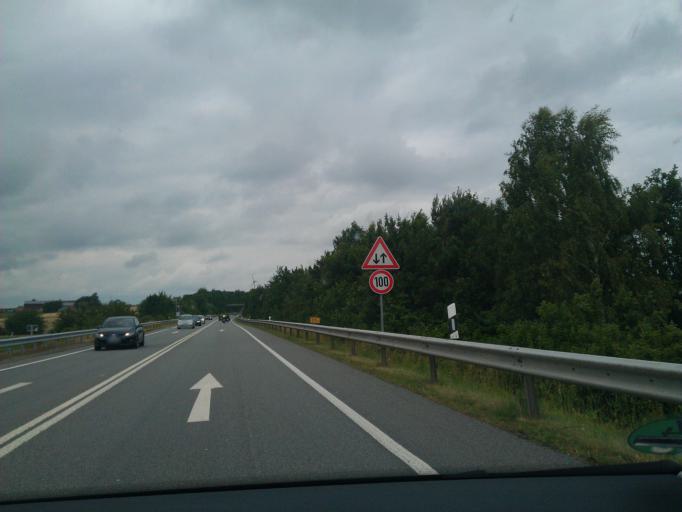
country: DE
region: Rheinland-Pfalz
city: Hermersberg
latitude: 49.3056
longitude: 7.6197
